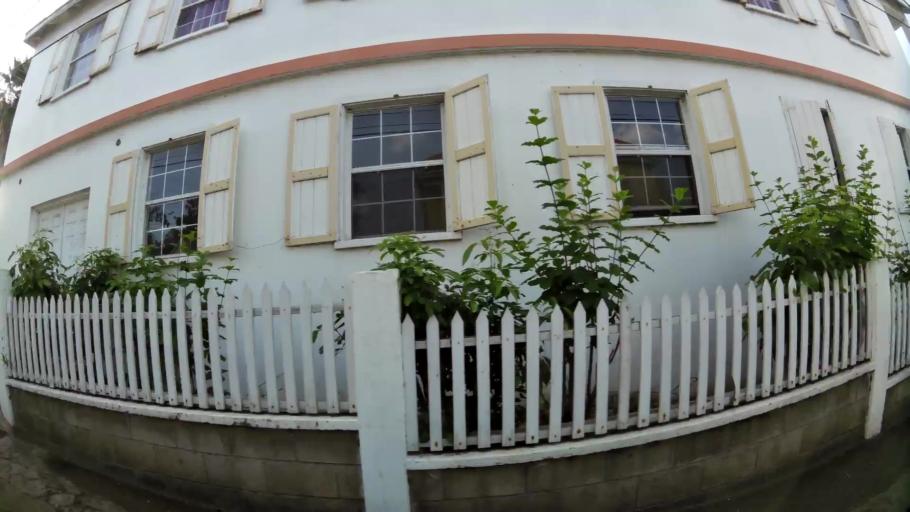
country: KN
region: Saint Paul Charlestown
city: Charlestown
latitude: 17.1399
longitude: -62.6287
